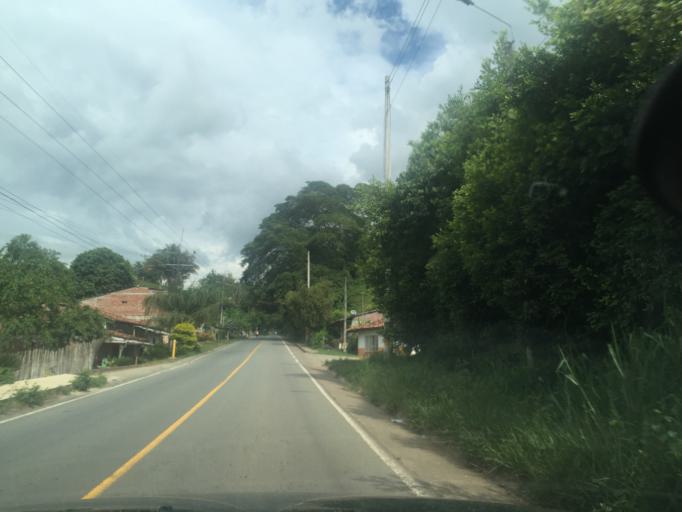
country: CO
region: Valle del Cauca
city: Caicedonia
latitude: 4.3411
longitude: -75.8417
